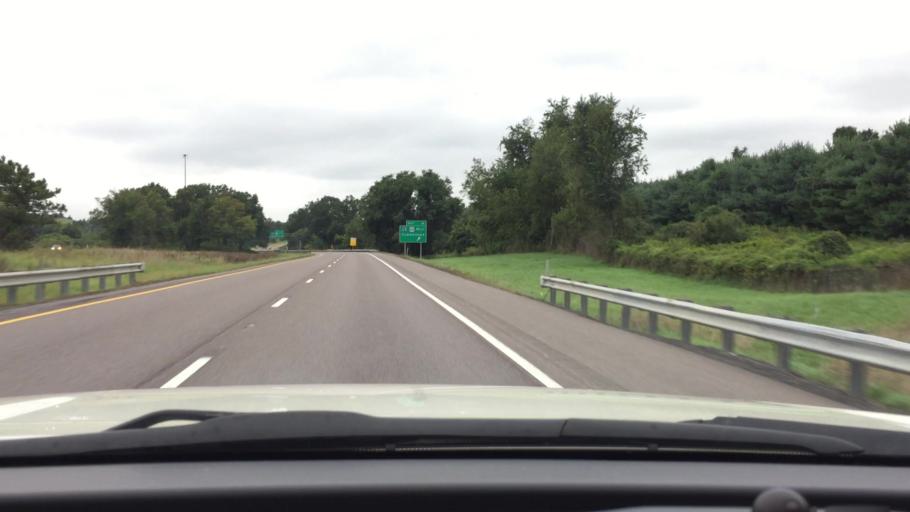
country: US
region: Maryland
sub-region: Washington County
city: Hancock
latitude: 39.7199
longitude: -78.1867
